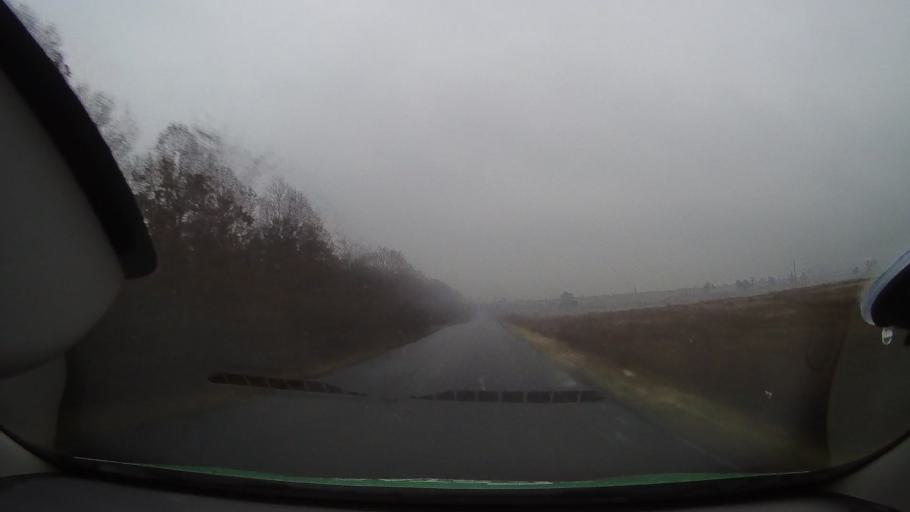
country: RO
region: Bihor
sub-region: Comuna Tinca
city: Gurbediu
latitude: 46.7776
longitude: 21.8776
